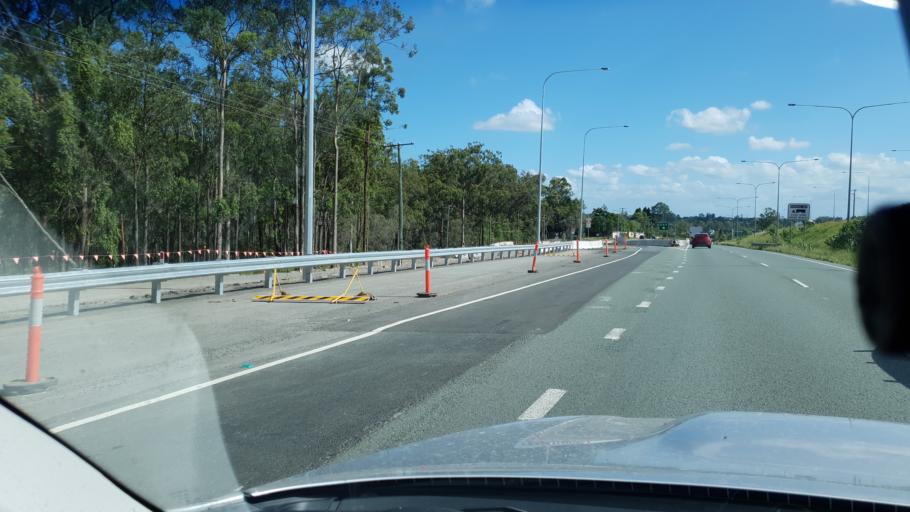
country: AU
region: Queensland
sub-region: Brisbane
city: Sunnybank Hills
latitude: -27.6516
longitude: 153.0408
